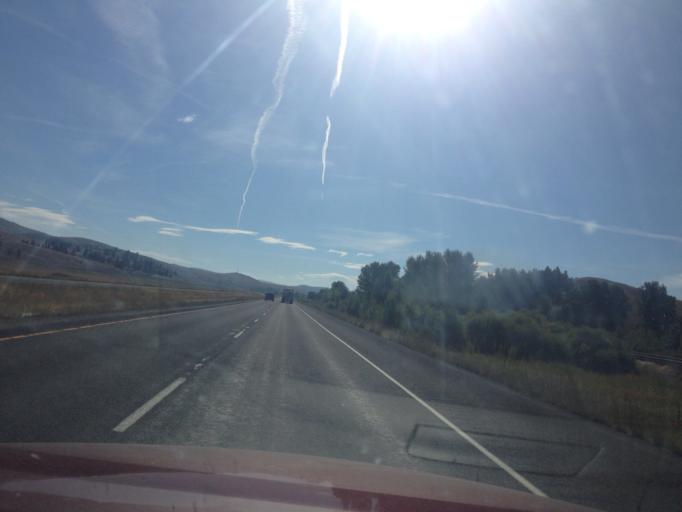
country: US
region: Montana
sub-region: Powell County
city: Deer Lodge
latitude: 46.6045
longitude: -112.9727
